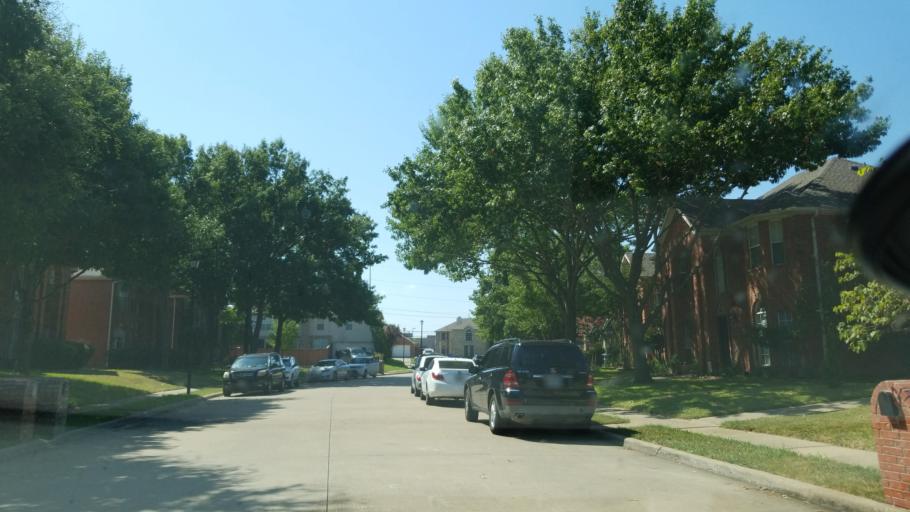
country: US
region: Texas
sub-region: Dallas County
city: Richardson
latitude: 32.9107
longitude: -96.7097
